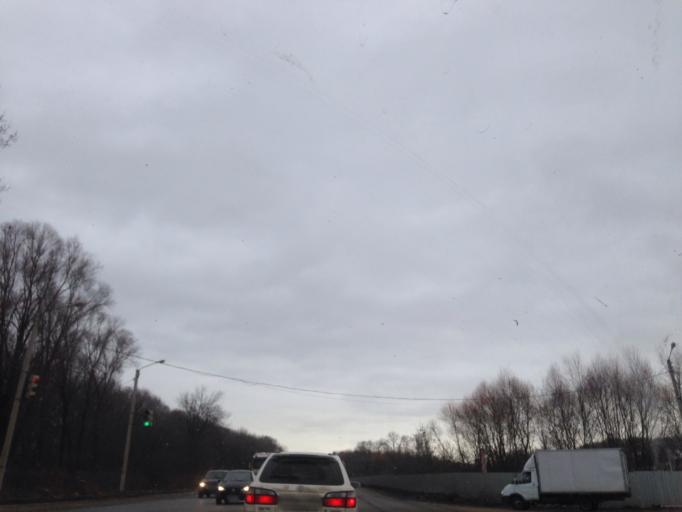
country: RU
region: Tula
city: Tula
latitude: 54.1440
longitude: 37.6547
